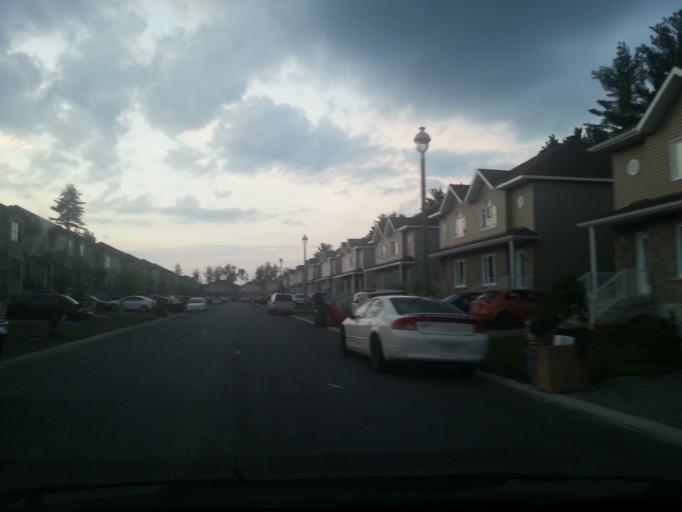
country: CA
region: Quebec
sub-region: Outaouais
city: Gatineau
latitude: 45.5079
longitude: -75.5708
